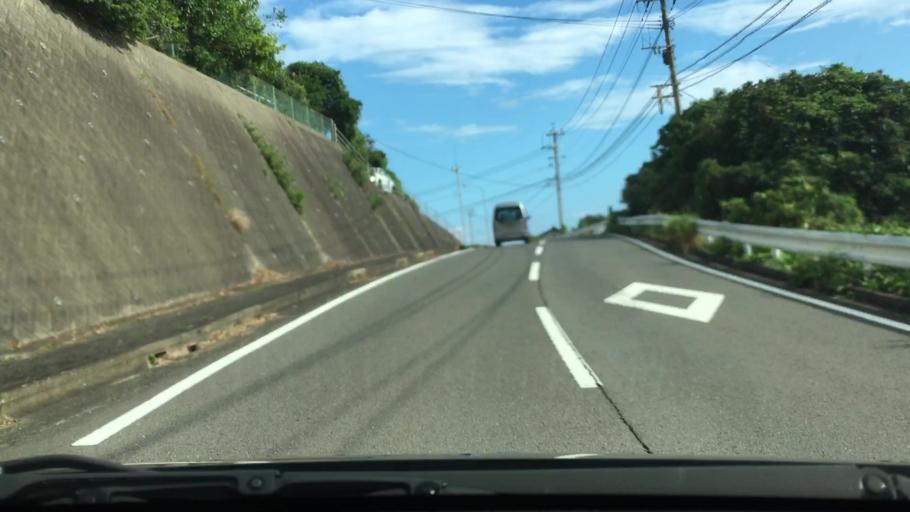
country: JP
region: Nagasaki
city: Togitsu
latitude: 32.8550
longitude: 129.6866
